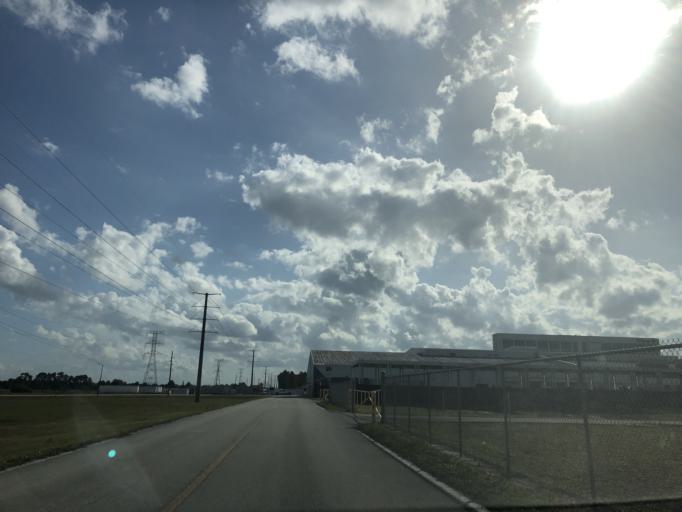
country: US
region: Florida
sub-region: Orange County
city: Williamsburg
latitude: 28.4304
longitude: -81.4544
